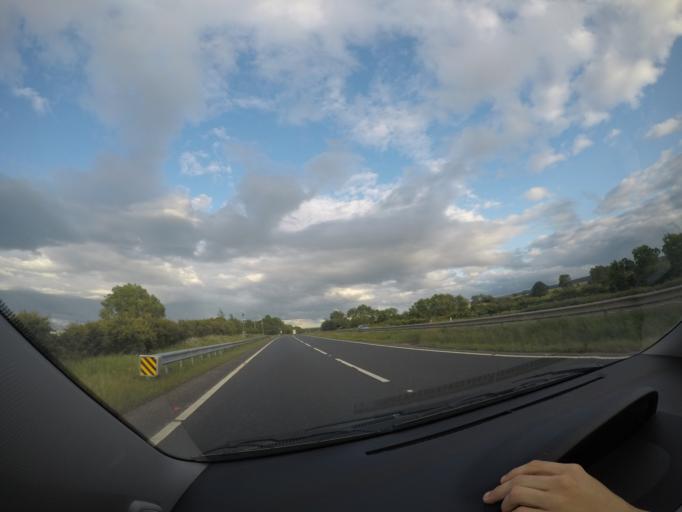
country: GB
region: England
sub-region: County Durham
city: Rokeby
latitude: 54.5059
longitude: -1.8473
